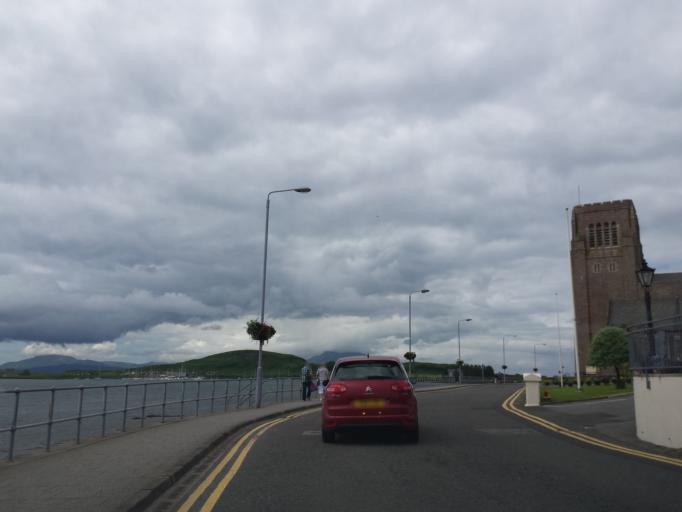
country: GB
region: Scotland
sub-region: Argyll and Bute
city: Oban
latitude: 56.4187
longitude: -5.4776
